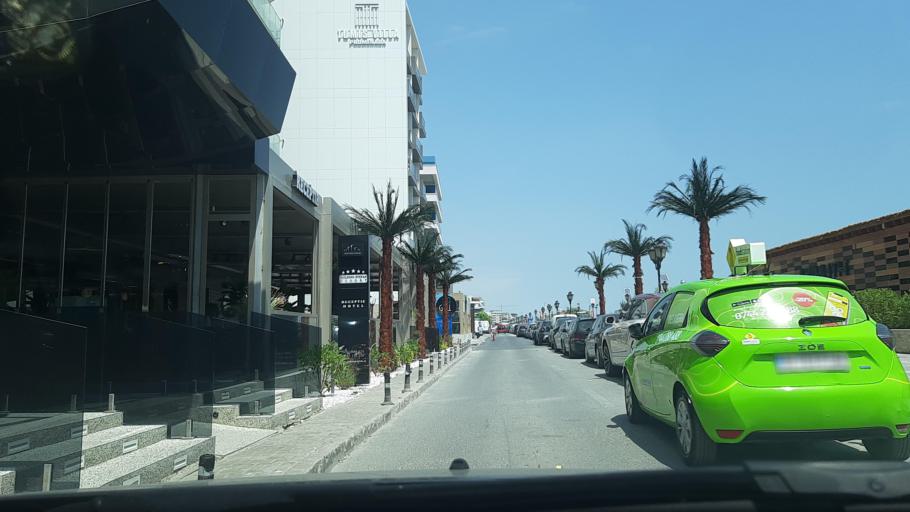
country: RO
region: Constanta
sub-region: Comuna Navodari
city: Navodari
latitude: 44.2940
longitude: 28.6241
